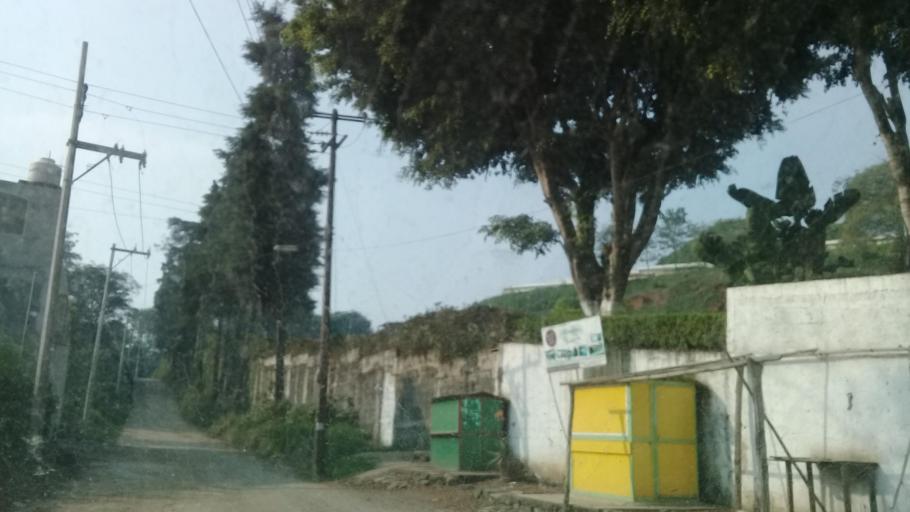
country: MX
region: Veracruz
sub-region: Xalapa
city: Lomas Verdes
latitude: 19.5001
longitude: -96.8999
